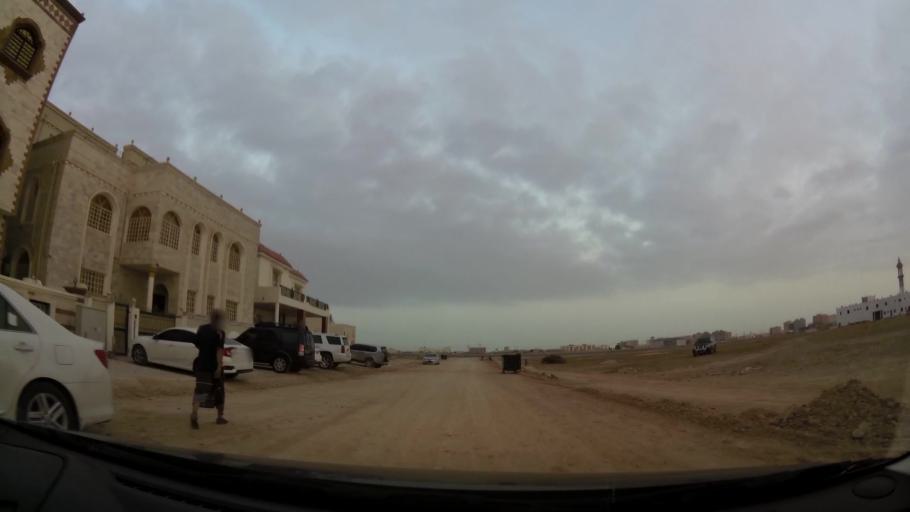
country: OM
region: Zufar
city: Salalah
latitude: 17.0366
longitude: 54.0317
